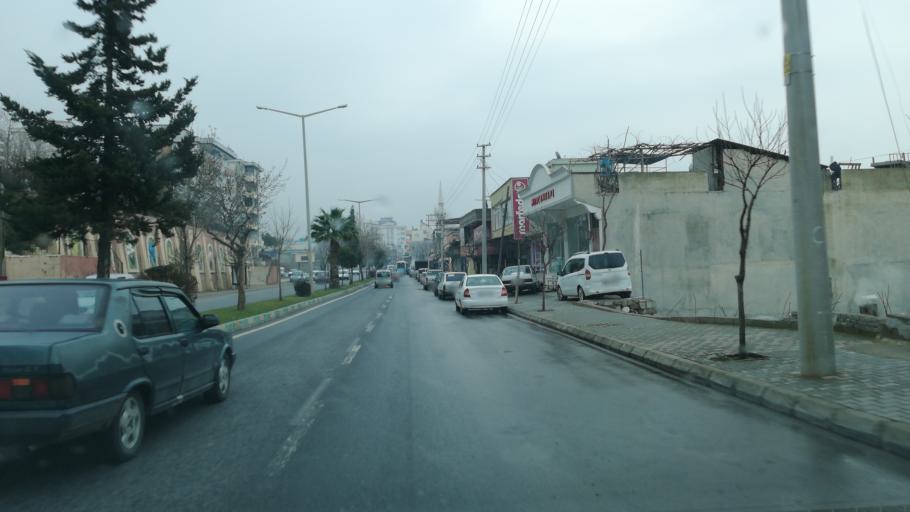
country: TR
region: Kahramanmaras
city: Kahramanmaras
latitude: 37.5816
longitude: 36.9598
